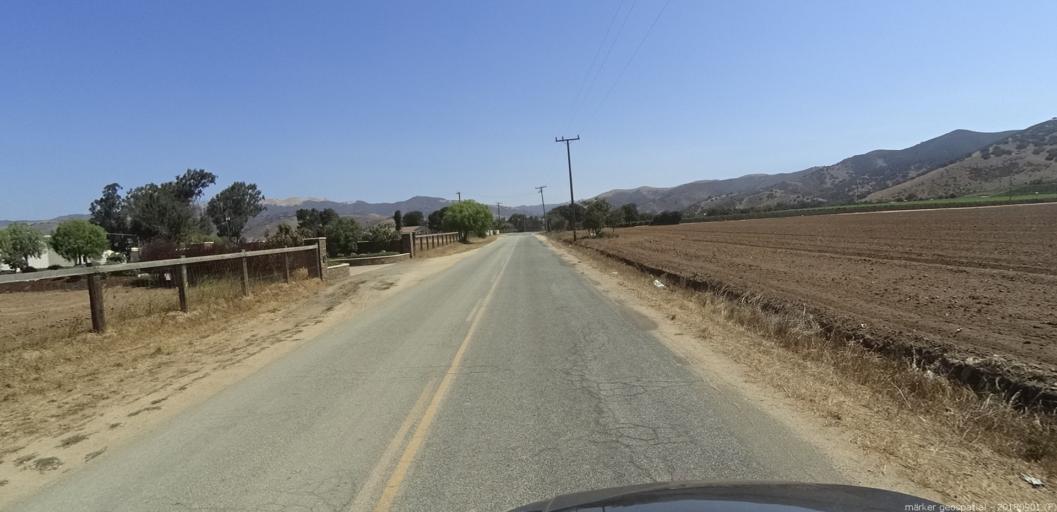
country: US
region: California
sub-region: Monterey County
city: Chualar
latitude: 36.5894
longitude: -121.4598
